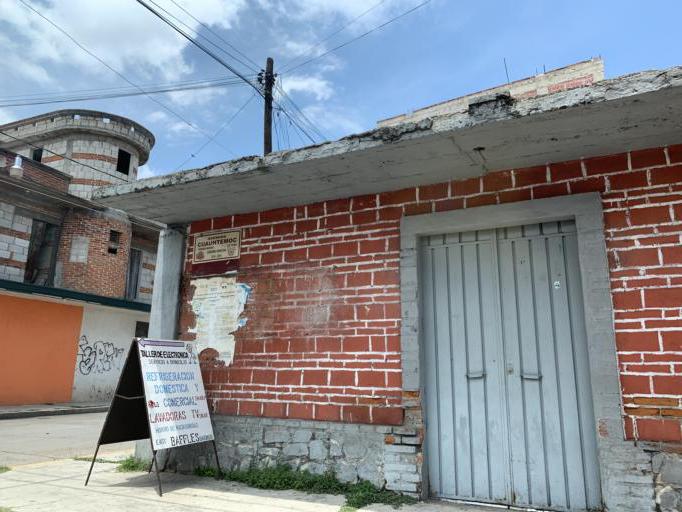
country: MX
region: Puebla
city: Huejotzingo
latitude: 19.1543
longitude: -98.4042
